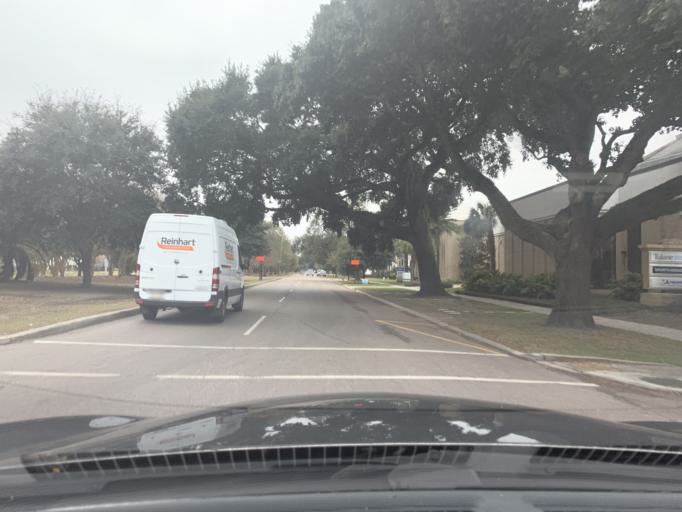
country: US
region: Louisiana
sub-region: Jefferson Parish
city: Metairie
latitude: 30.0185
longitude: -90.1066
